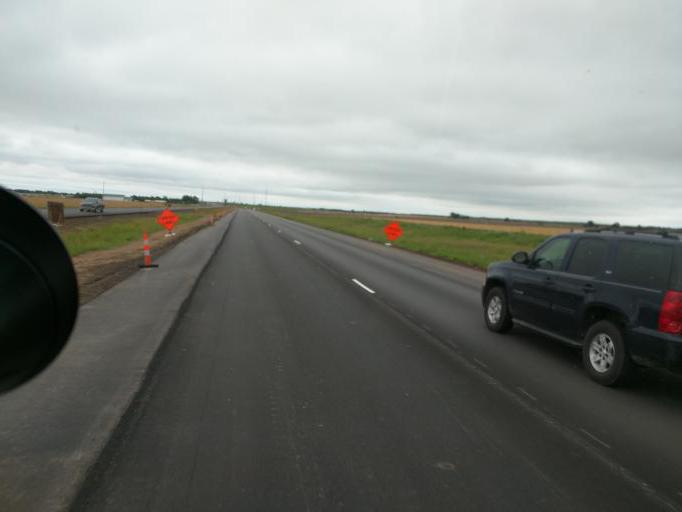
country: US
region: Kansas
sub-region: Reno County
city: South Hutchinson
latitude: 38.0137
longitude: -97.9853
